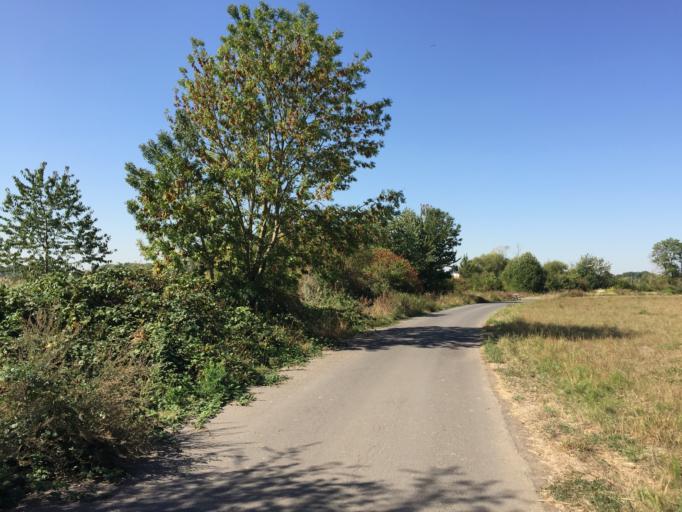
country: DE
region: Hesse
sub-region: Regierungsbezirk Giessen
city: Hungen
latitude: 50.4471
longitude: 8.9157
